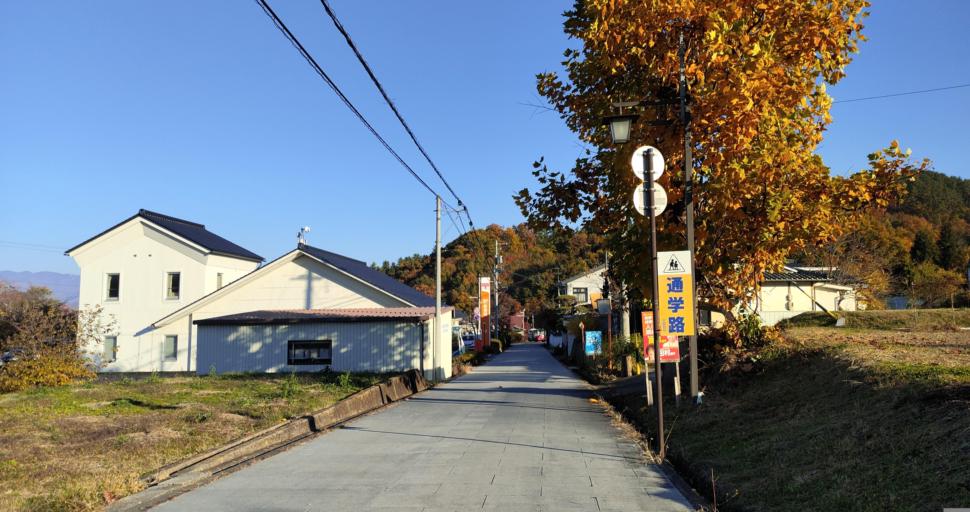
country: JP
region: Nagano
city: Kamimaruko
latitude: 36.3525
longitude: 138.1579
